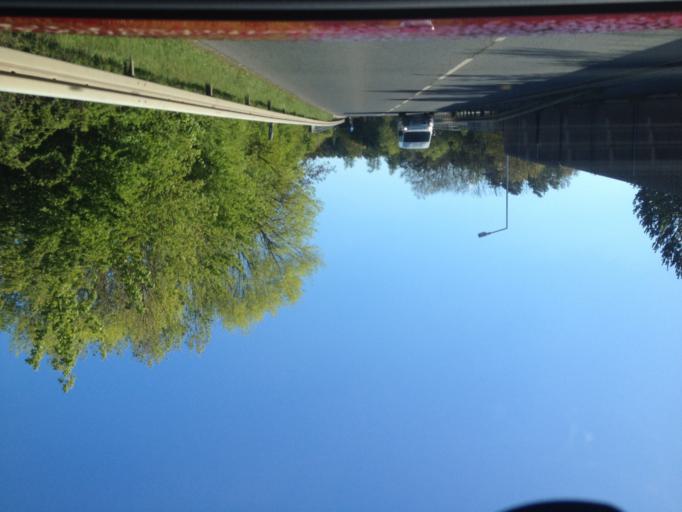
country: DE
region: Bavaria
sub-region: Regierungsbezirk Mittelfranken
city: Lauf an der Pegnitz
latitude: 49.5017
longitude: 11.2863
